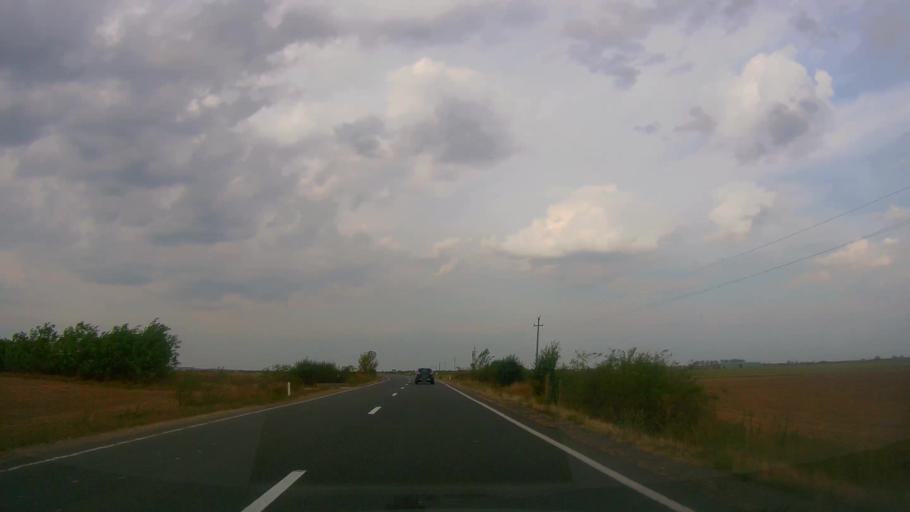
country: RO
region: Satu Mare
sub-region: Comuna Beltiug
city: Beltiug
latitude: 47.5410
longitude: 22.8192
